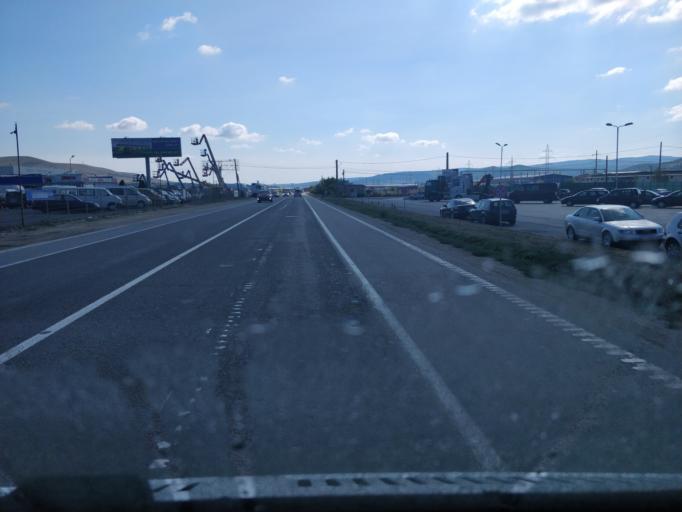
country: RO
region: Cluj
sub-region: Comuna Floresti
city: Luna de Sus
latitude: 46.7508
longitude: 23.4314
